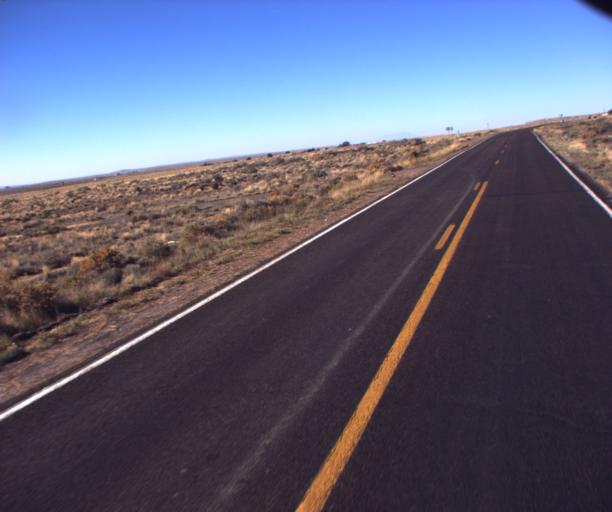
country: US
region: Arizona
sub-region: Navajo County
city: First Mesa
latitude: 35.7932
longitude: -110.4824
